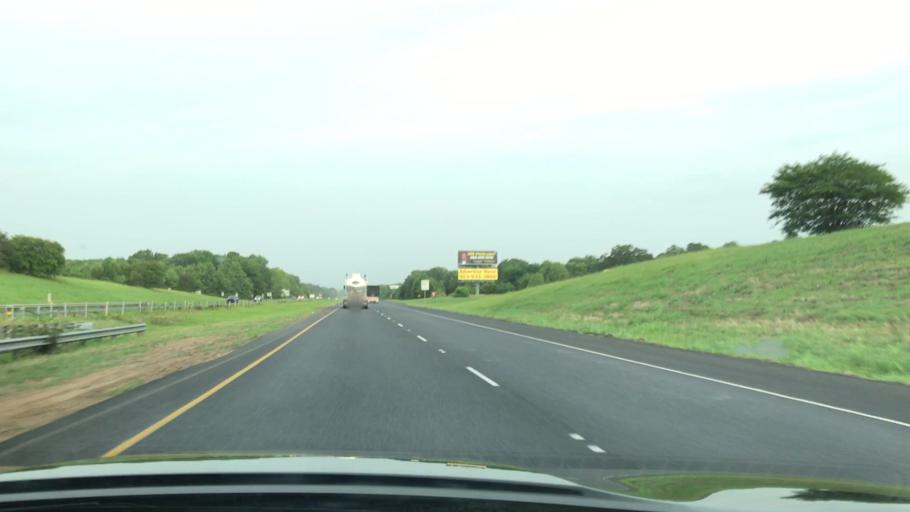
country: US
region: Louisiana
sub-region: Caddo Parish
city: Greenwood
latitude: 32.4441
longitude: -93.9497
